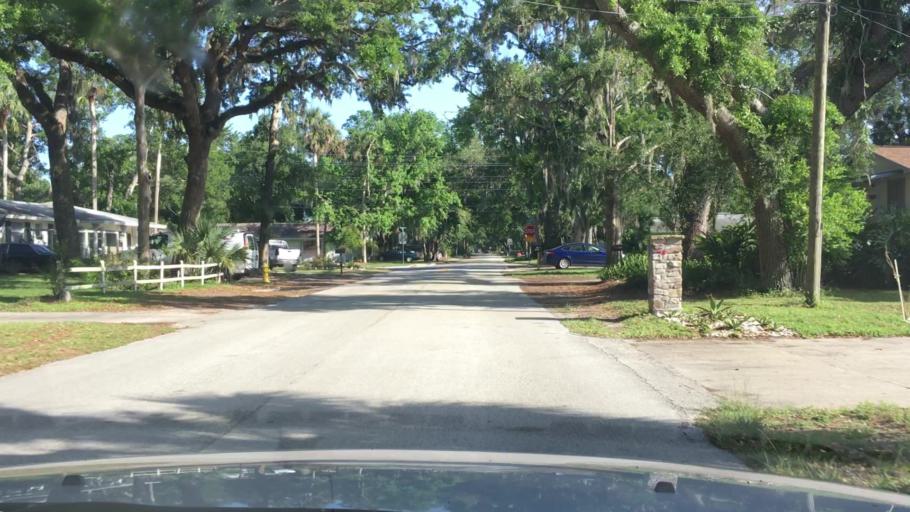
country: US
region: Florida
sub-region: Volusia County
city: Ormond Beach
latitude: 29.2690
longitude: -81.0647
